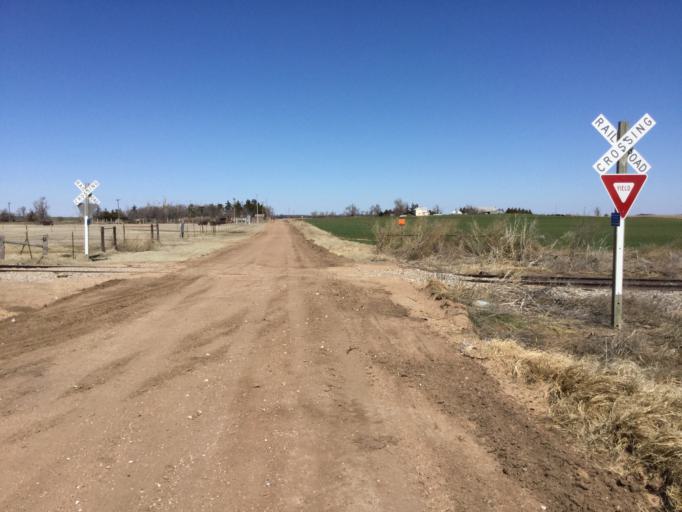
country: US
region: Kansas
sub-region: Barber County
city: Medicine Lodge
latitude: 37.4654
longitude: -98.5469
